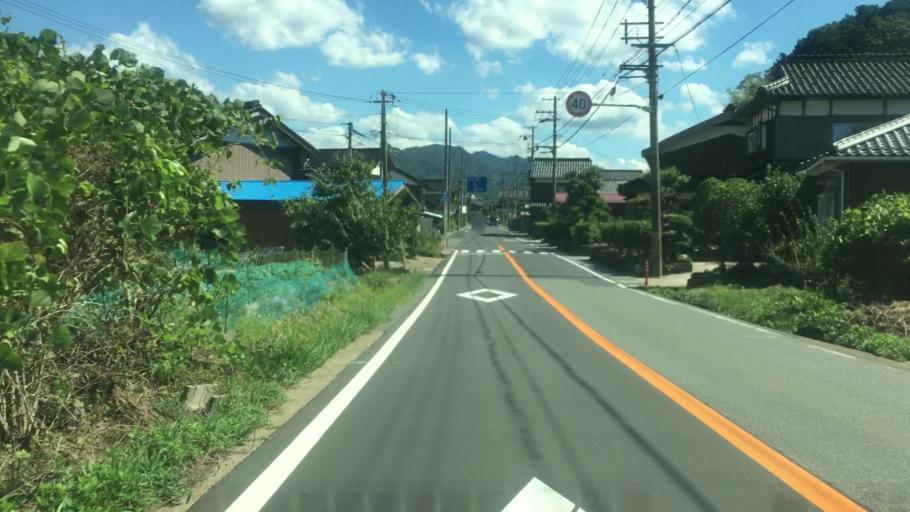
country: JP
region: Hyogo
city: Toyooka
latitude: 35.5905
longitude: 134.9238
